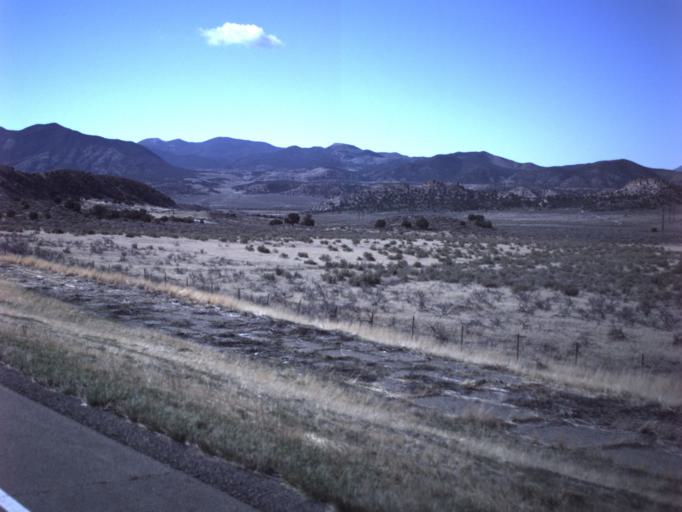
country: US
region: Utah
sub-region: Sanpete County
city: Gunnison
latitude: 39.3748
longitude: -111.9284
